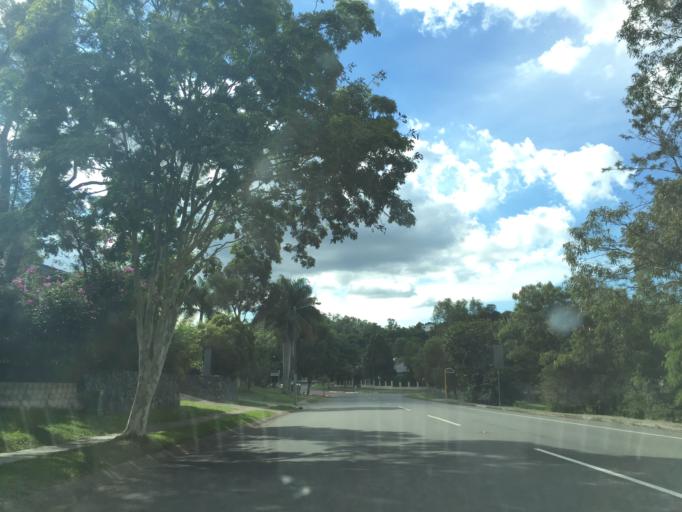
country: AU
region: Queensland
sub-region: Moreton Bay
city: Ferny Hills
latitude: -27.4369
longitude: 152.9351
